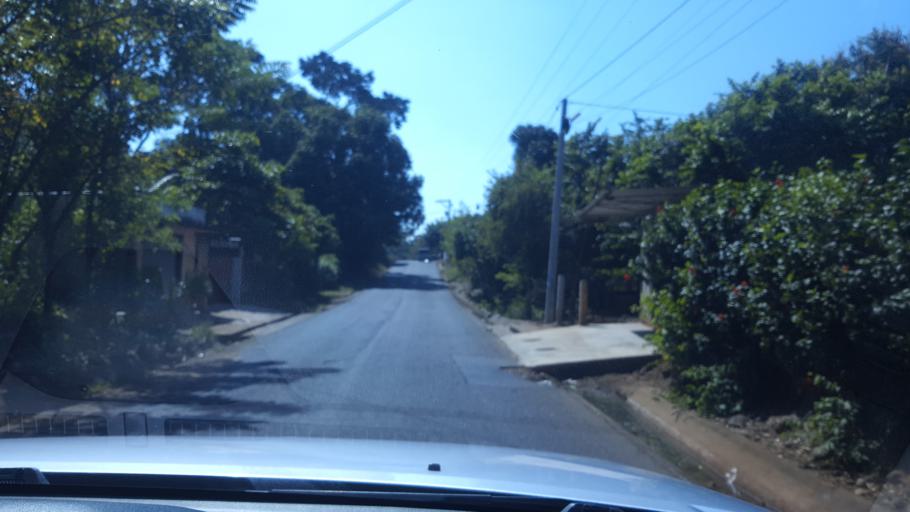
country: GT
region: Quetzaltenango
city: Flores Costa Cuca
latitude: 14.6338
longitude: -91.9270
